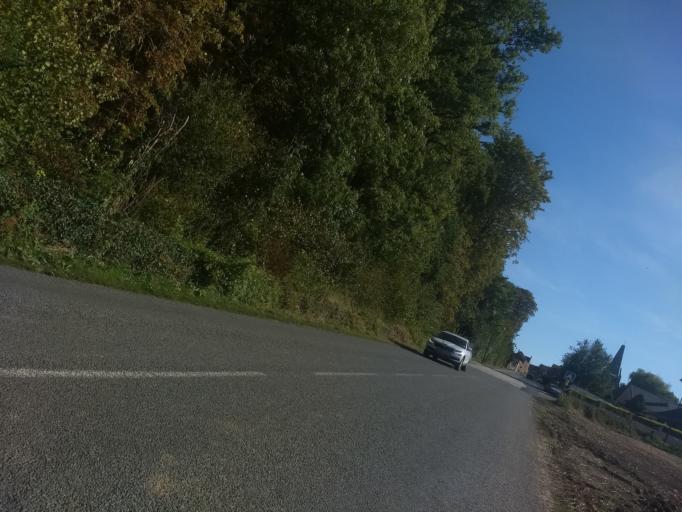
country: FR
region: Nord-Pas-de-Calais
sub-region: Departement du Pas-de-Calais
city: Roeux
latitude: 50.2742
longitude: 2.8928
